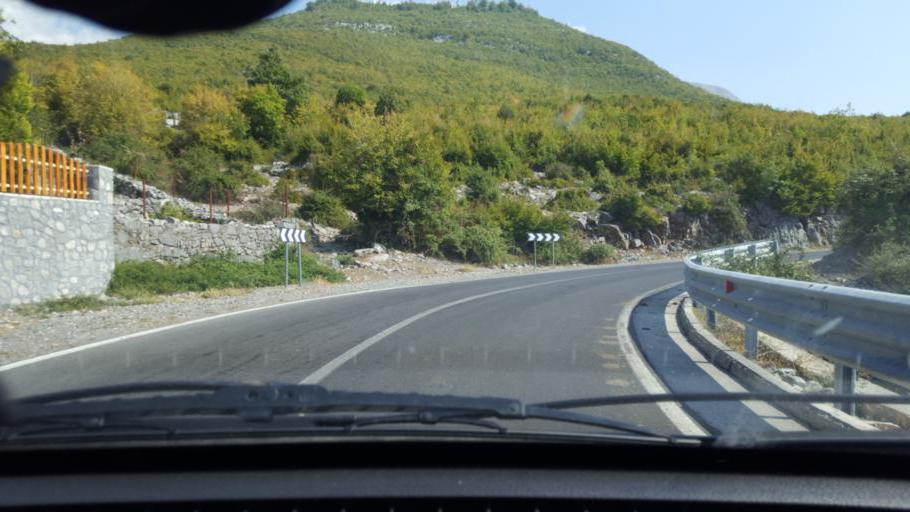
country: AL
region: Shkoder
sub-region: Rrethi i Malesia e Madhe
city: Kastrat
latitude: 42.3836
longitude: 19.4941
